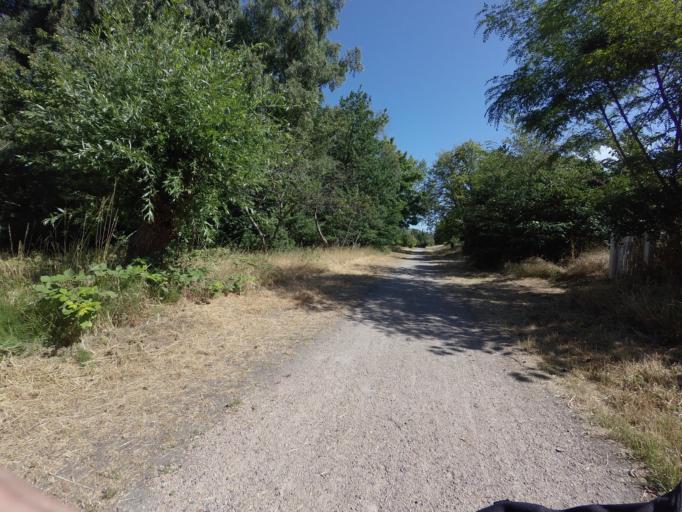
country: SE
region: Skane
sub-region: Vellinge Kommun
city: Skanor med Falsterbo
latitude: 55.3966
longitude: 12.8307
